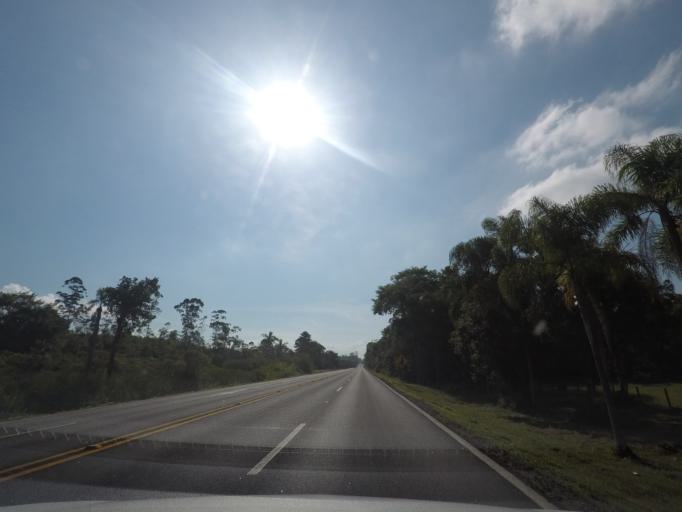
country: BR
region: Parana
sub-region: Pontal Do Parana
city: Pontal do Parana
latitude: -25.6169
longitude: -48.6018
